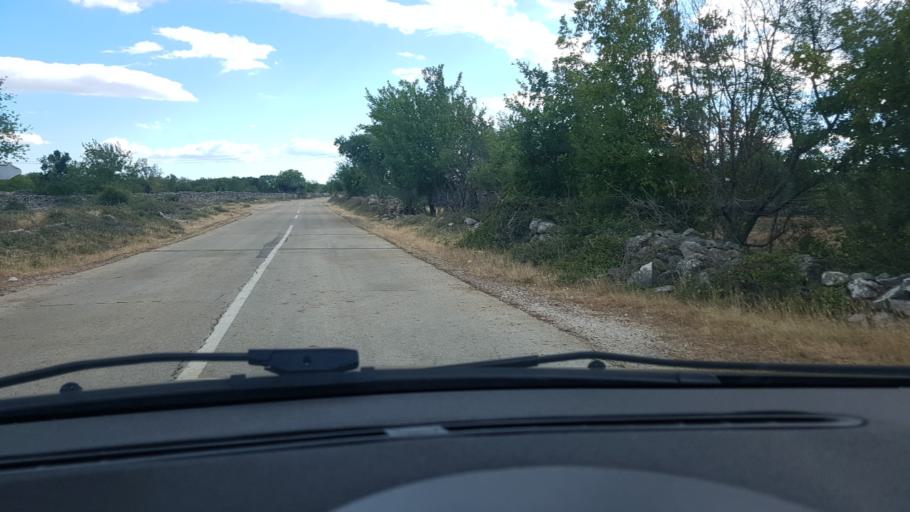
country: HR
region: Sibensko-Kniniska
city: Kistanje
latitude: 44.0615
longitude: 15.9313
